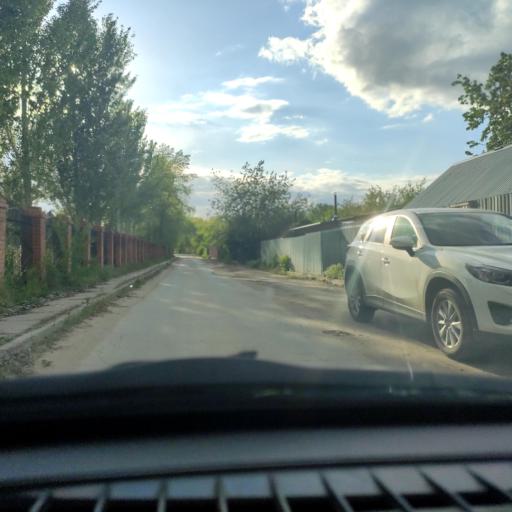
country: RU
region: Samara
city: Zhigulevsk
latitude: 53.4496
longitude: 49.5371
